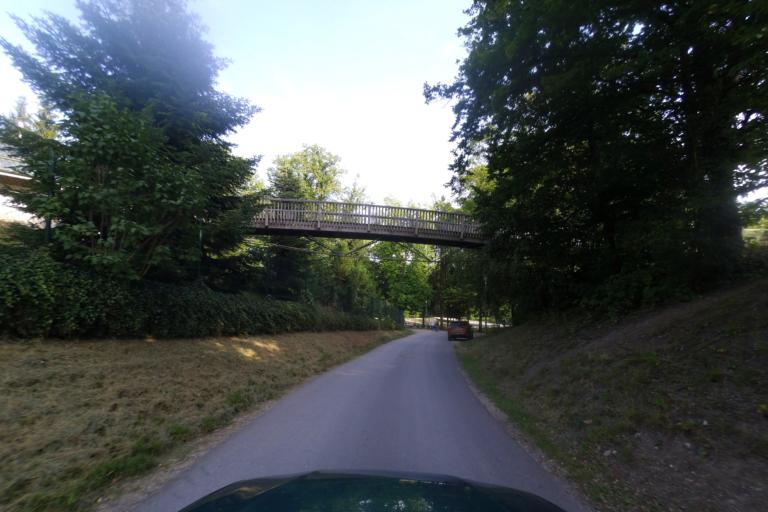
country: DE
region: Bavaria
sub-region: Swabia
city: Lauingen
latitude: 48.5662
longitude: 10.4282
